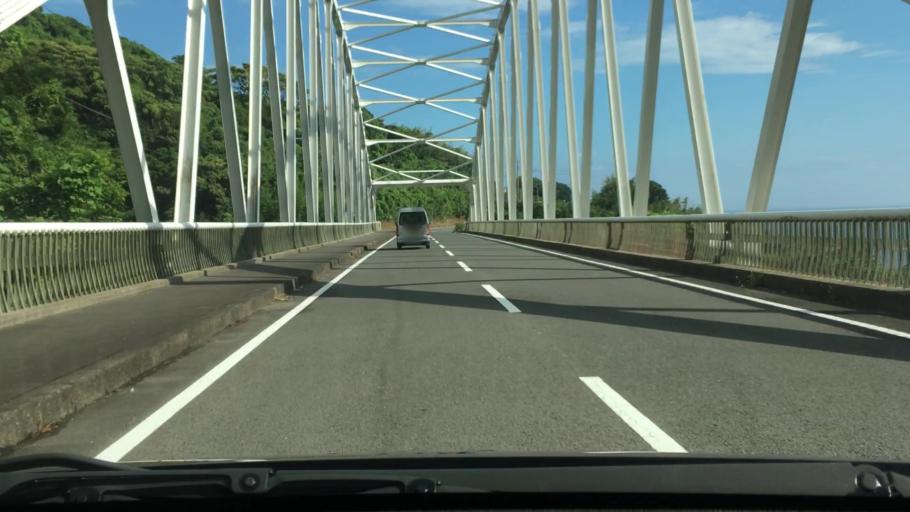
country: JP
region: Nagasaki
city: Togitsu
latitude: 32.8577
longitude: 129.6859
